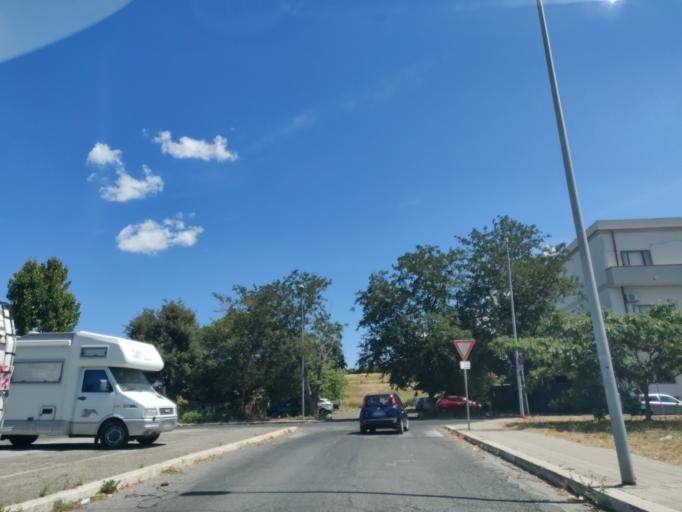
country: IT
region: Latium
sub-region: Citta metropolitana di Roma Capitale
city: Civitavecchia
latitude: 42.1023
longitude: 11.7977
